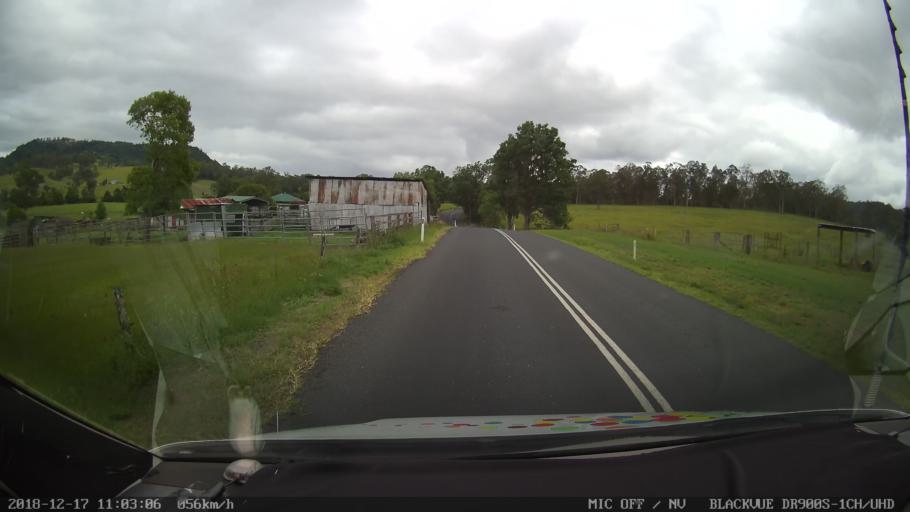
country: AU
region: New South Wales
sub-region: Kyogle
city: Kyogle
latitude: -28.8088
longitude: 152.6359
